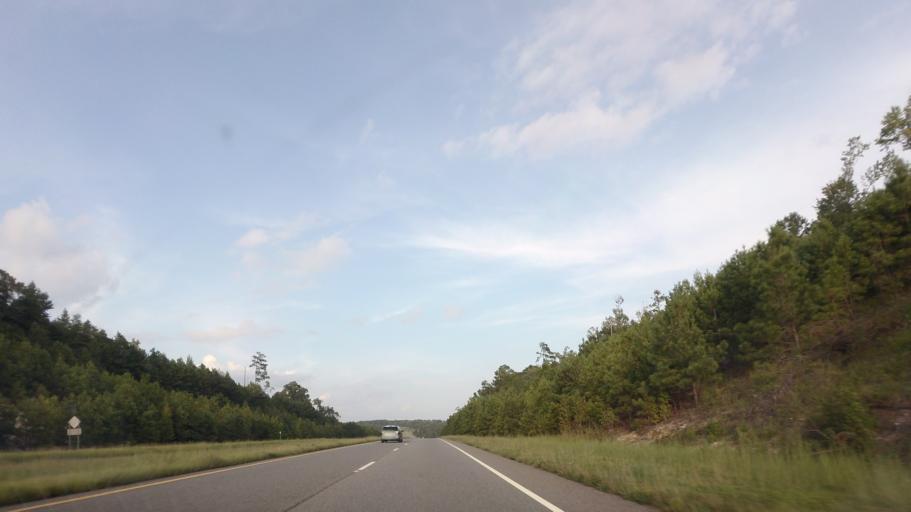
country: US
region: Georgia
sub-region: Wilkinson County
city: Gordon
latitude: 32.8543
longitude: -83.3939
